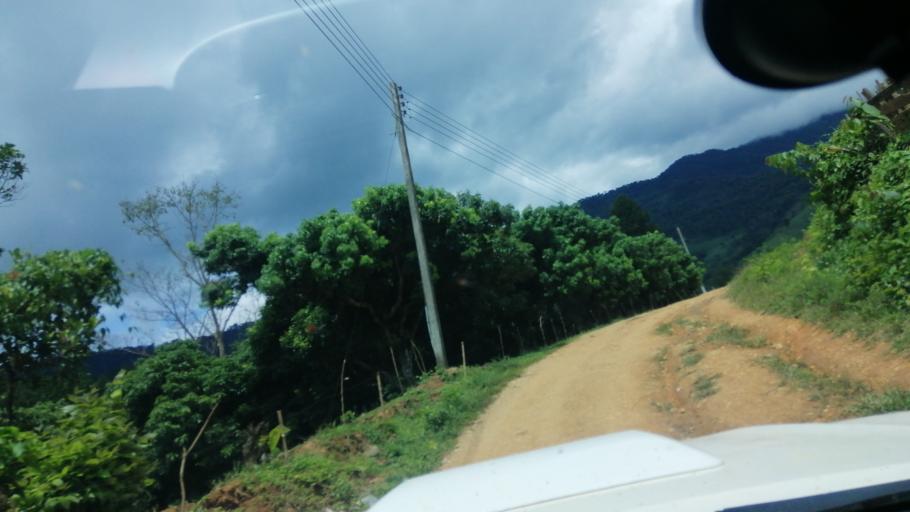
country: TH
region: Phayao
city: Phu Sang
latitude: 19.7452
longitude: 100.4297
